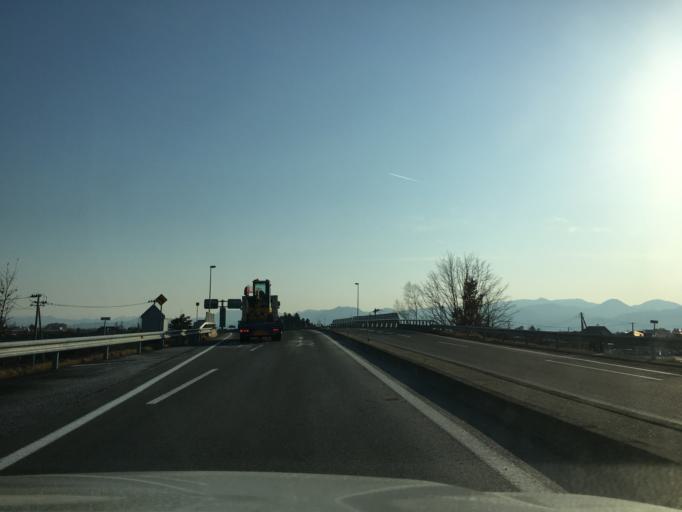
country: JP
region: Yamagata
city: Tendo
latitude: 38.3088
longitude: 140.3123
